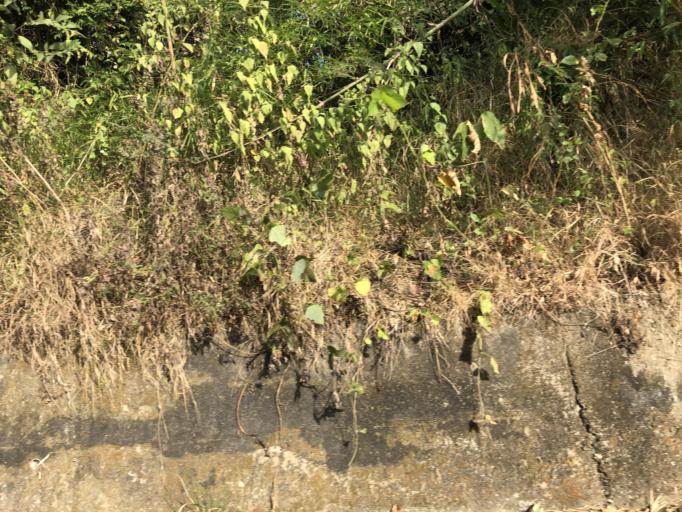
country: TW
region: Taiwan
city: Yujing
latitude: 23.0531
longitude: 120.4008
